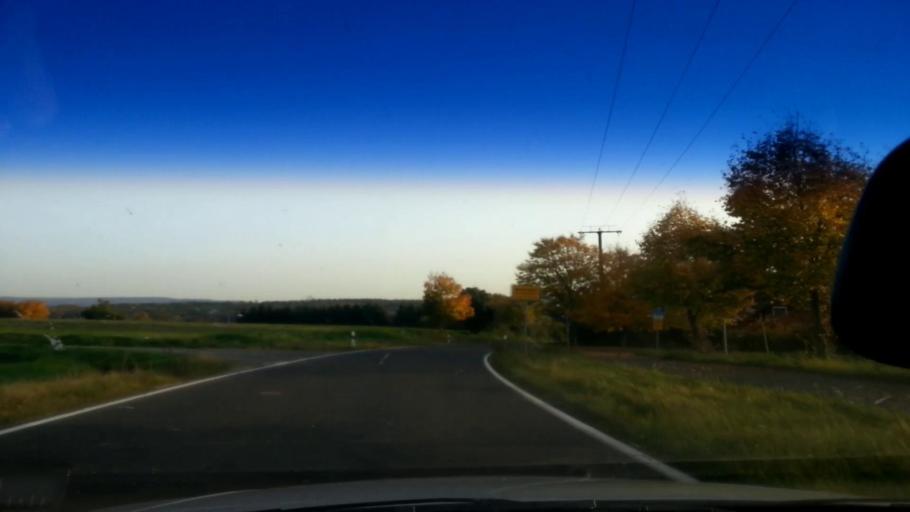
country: DE
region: Bavaria
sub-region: Upper Franconia
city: Memmelsdorf
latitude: 49.9459
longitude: 10.9563
